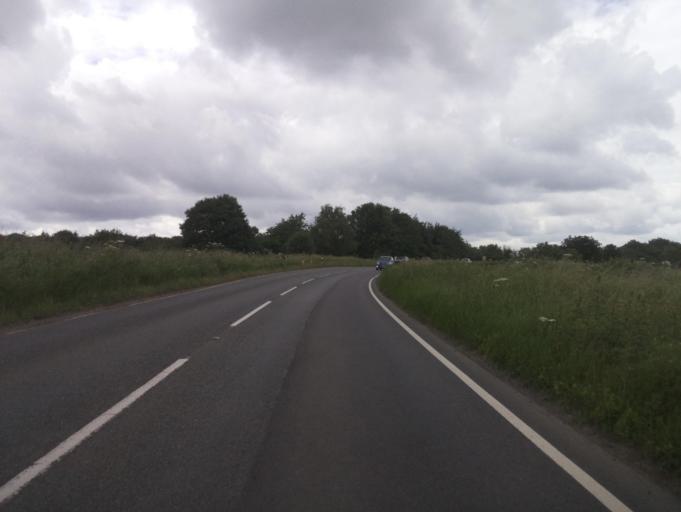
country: GB
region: England
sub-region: South Gloucestershire
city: Cold Ashton
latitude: 51.4288
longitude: -2.4028
